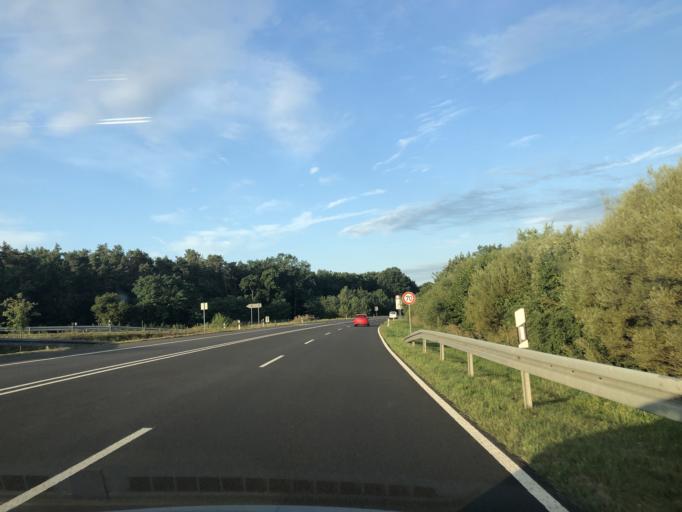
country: DE
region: Brandenburg
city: Mullrose
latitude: 52.2368
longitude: 14.3929
